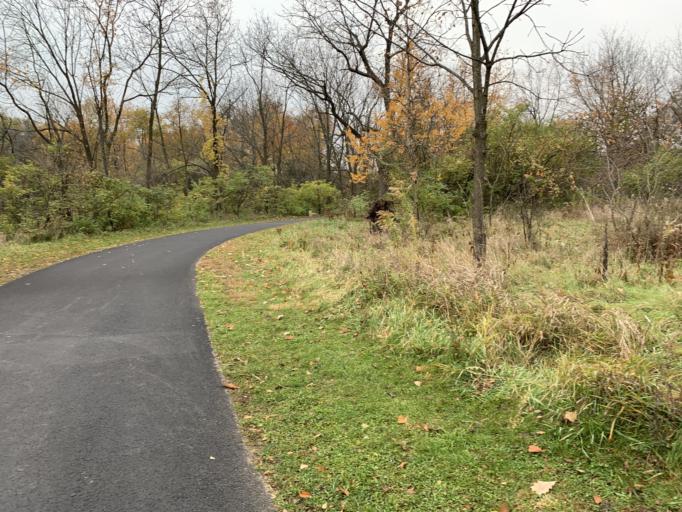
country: US
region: Illinois
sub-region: Will County
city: Plainfield
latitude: 41.6082
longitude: -88.1901
